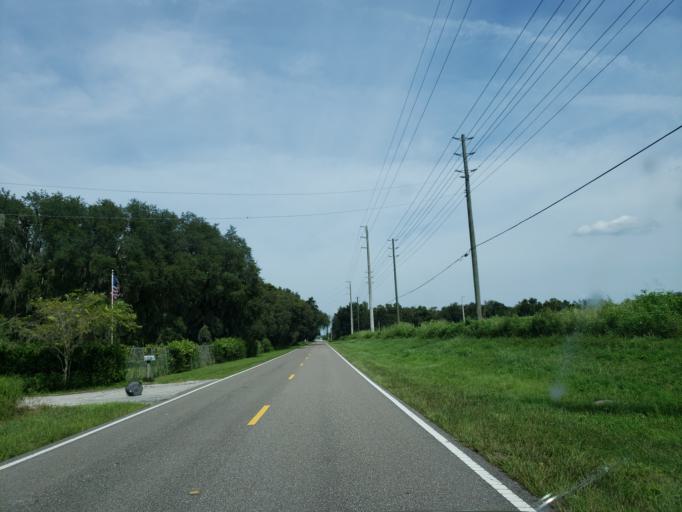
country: US
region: Florida
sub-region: Pasco County
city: Wesley Chapel
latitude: 28.2780
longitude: -82.3082
